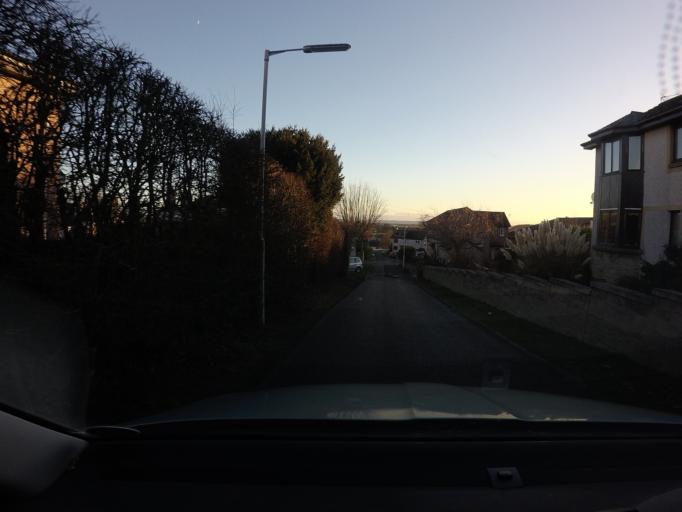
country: GB
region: Scotland
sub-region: Fife
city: Tayport
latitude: 56.4466
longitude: -2.8854
